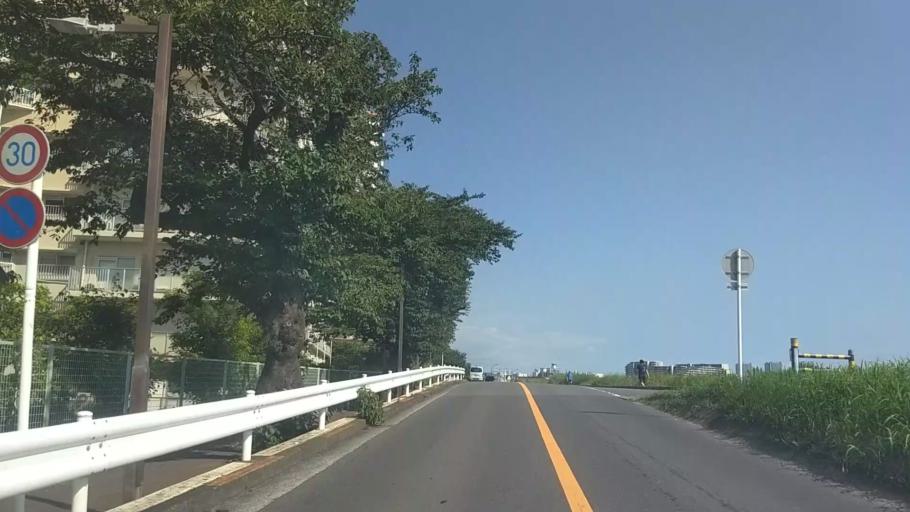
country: JP
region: Kanagawa
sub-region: Kawasaki-shi
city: Kawasaki
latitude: 35.5555
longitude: 139.7016
